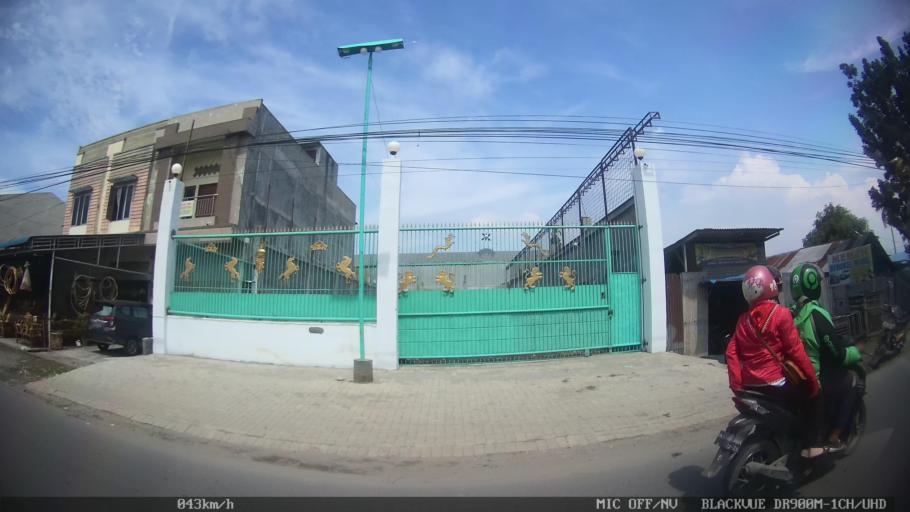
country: ID
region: North Sumatra
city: Labuhan Deli
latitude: 3.6698
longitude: 98.6558
